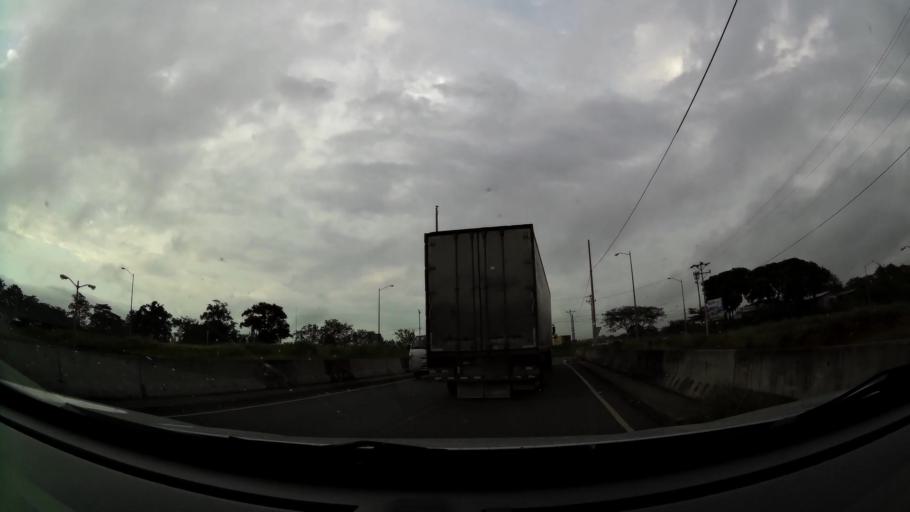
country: CR
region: Heredia
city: Colon
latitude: 9.9646
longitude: -84.2797
